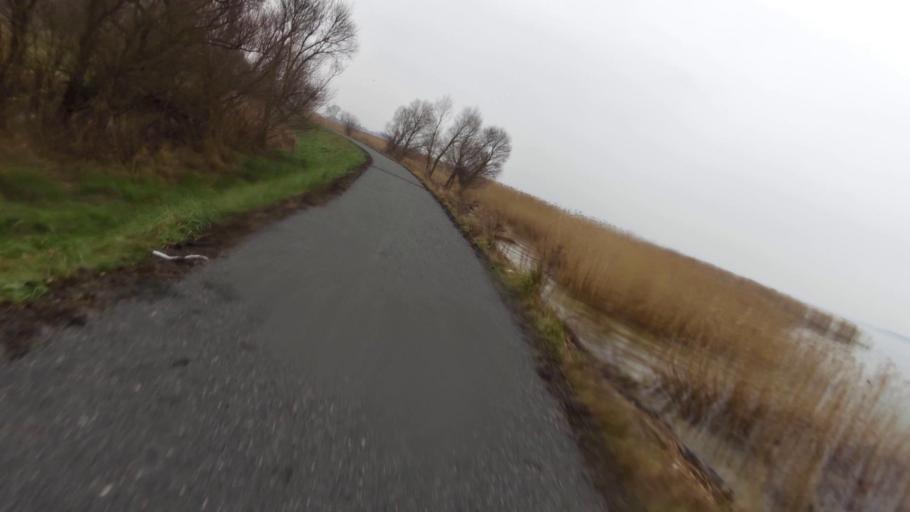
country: PL
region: West Pomeranian Voivodeship
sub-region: Powiat policki
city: Police
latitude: 53.4879
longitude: 14.6943
